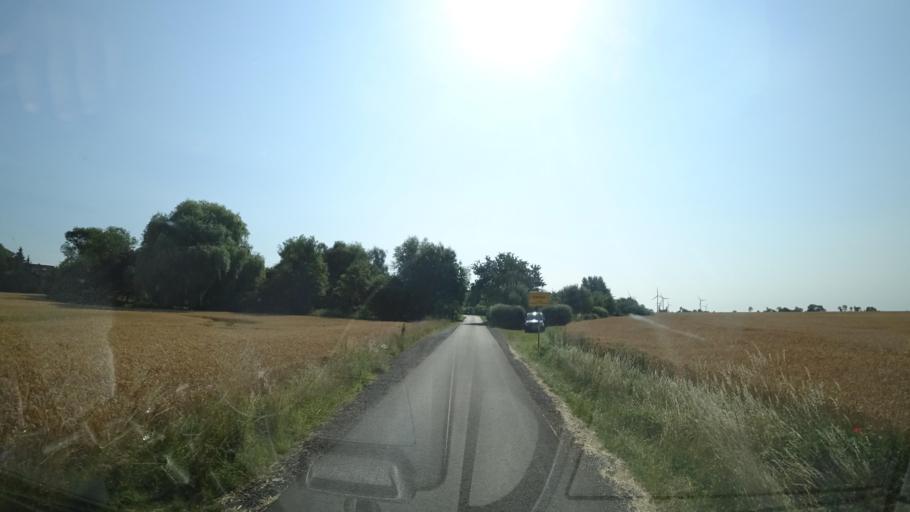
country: DE
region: Mecklenburg-Vorpommern
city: Wusterhusen
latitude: 54.1191
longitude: 13.5654
